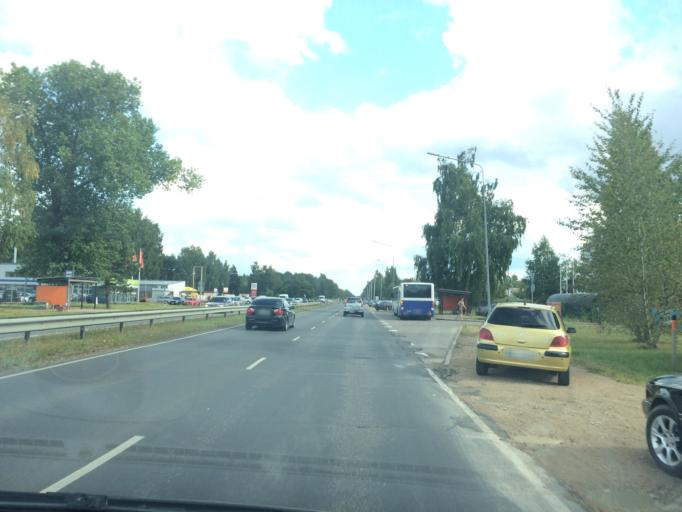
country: LV
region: Kekava
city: Kekava
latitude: 56.8870
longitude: 24.2340
